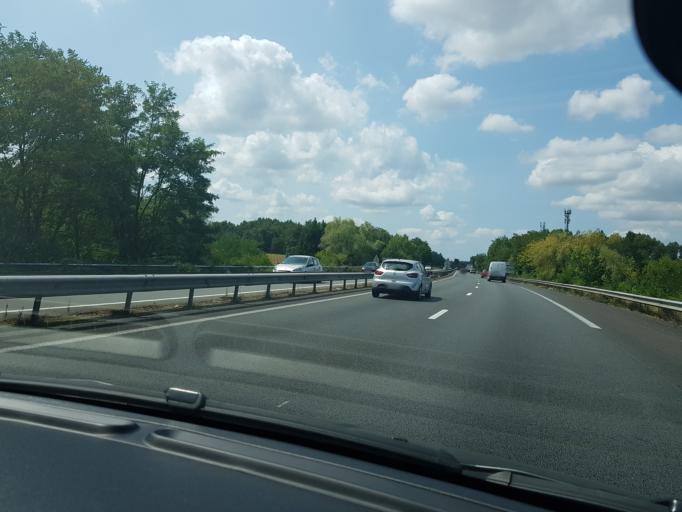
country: FR
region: Aquitaine
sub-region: Departement de la Gironde
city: Arveyres
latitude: 44.8799
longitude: -0.2987
